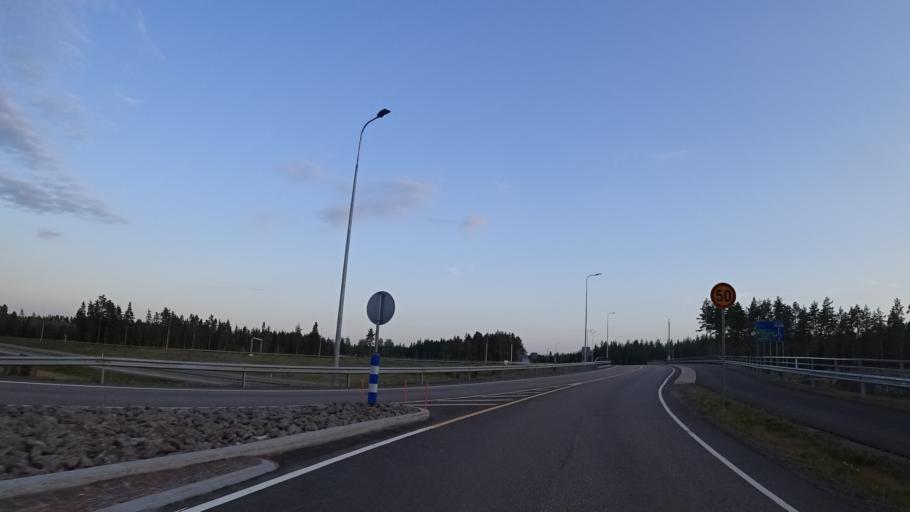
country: FI
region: Kymenlaakso
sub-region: Kotka-Hamina
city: Virojoki
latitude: 60.6062
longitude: 27.7045
